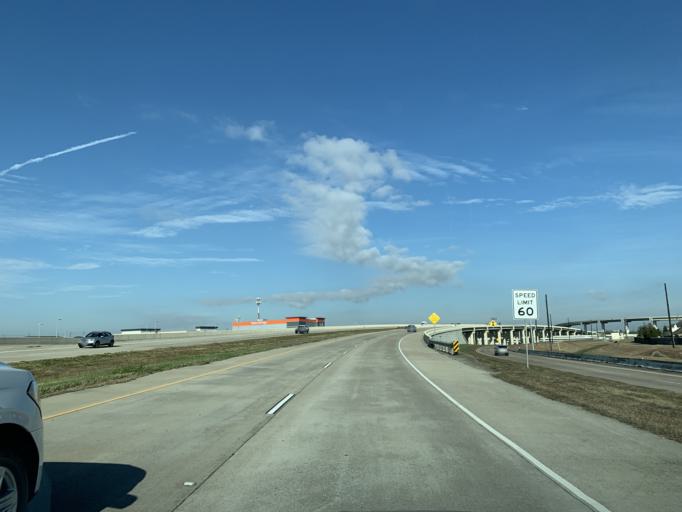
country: US
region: Texas
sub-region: Fort Bend County
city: Cinco Ranch
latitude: 29.6961
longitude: -95.7740
